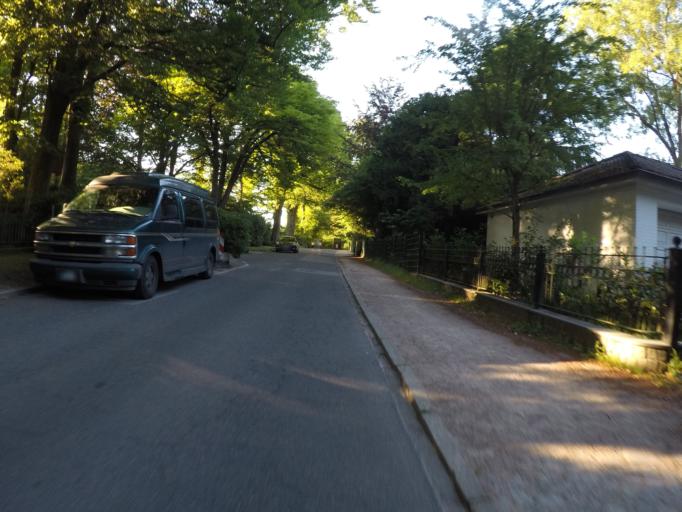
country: DE
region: Hamburg
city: Wohldorf-Ohlstedt
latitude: 53.6863
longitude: 10.1147
